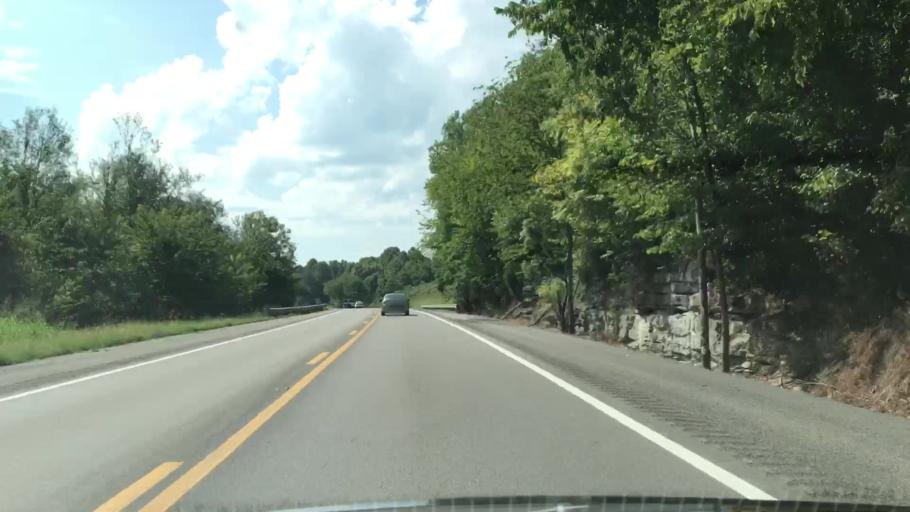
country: US
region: Tennessee
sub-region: Sumner County
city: Westmoreland
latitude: 36.6202
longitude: -86.2367
